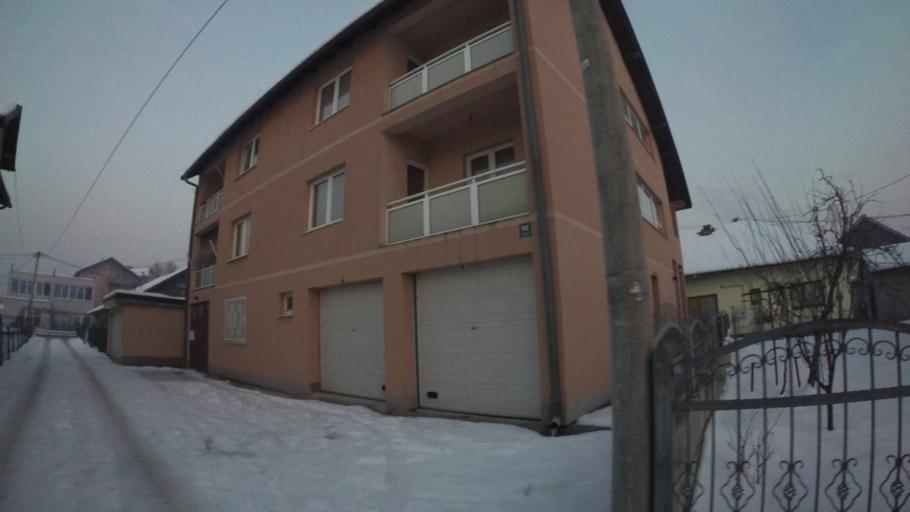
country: BA
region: Federation of Bosnia and Herzegovina
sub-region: Kanton Sarajevo
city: Sarajevo
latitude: 43.8318
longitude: 18.3224
